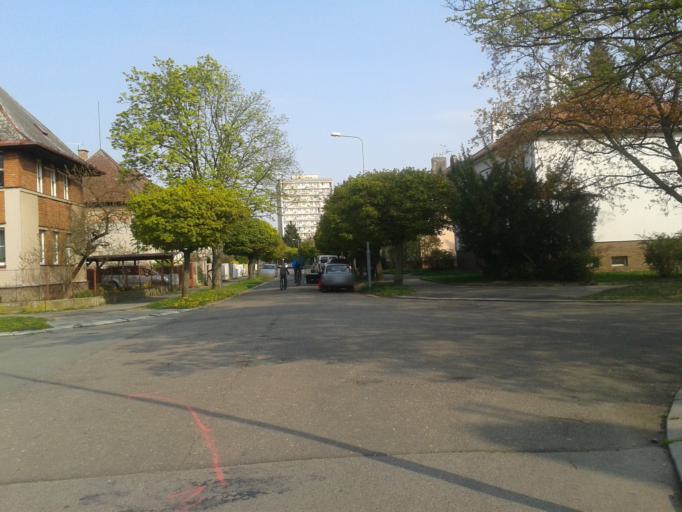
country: CZ
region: Pardubicky
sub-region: Okres Pardubice
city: Pardubice
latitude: 50.0376
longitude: 15.7928
